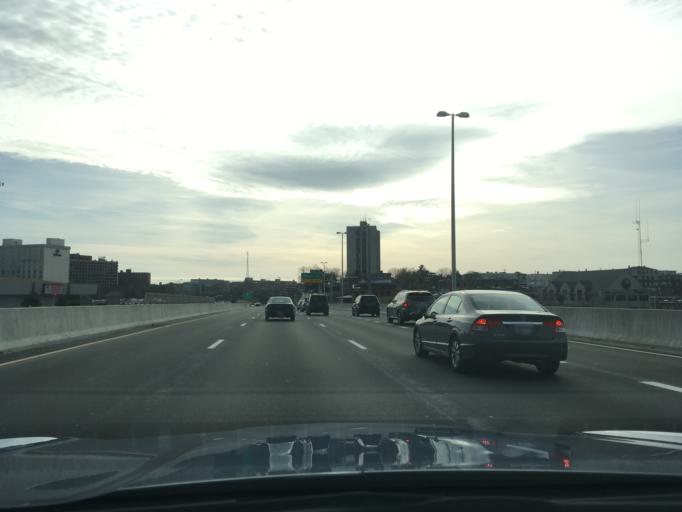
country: US
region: Rhode Island
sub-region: Providence County
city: Providence
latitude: 41.8266
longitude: -71.4191
